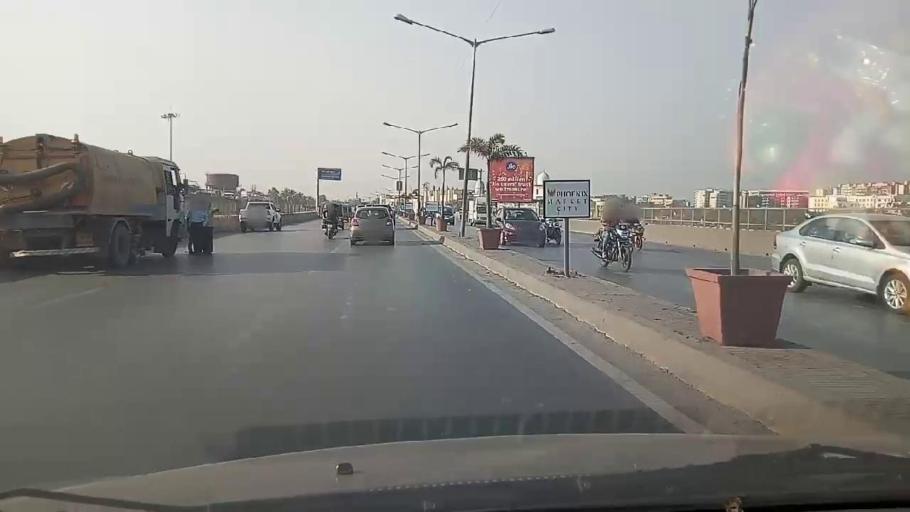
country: IN
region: Maharashtra
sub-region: Mumbai Suburban
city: Mumbai
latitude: 19.0699
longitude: 72.8865
